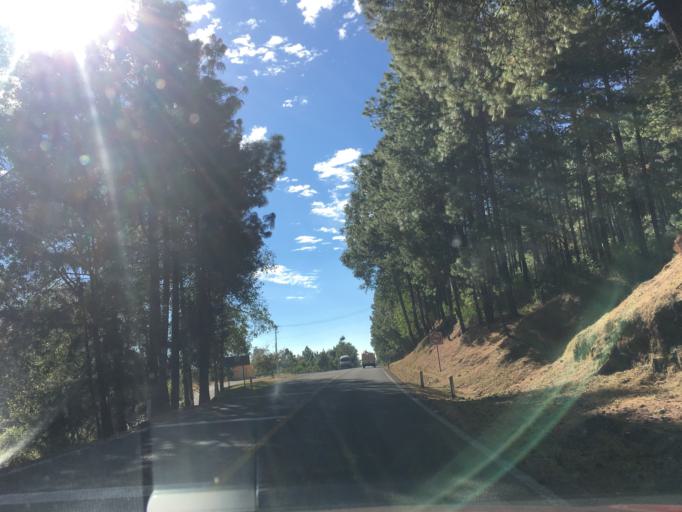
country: MX
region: Michoacan
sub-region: Hidalgo
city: Tierras Coloradas (San Pedro)
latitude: 19.7329
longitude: -100.7581
